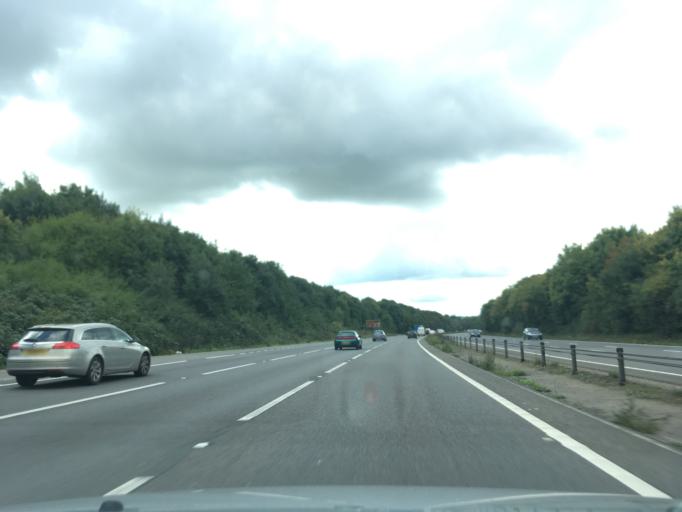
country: GB
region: England
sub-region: Surrey
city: Guildford
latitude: 51.2594
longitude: -0.5542
